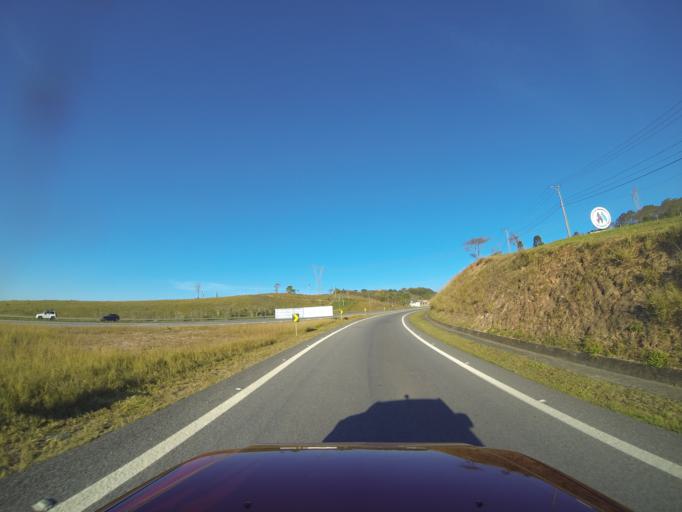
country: BR
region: Sao Paulo
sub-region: Sao Jose Dos Campos
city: Sao Jose dos Campos
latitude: -23.2695
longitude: -45.8181
